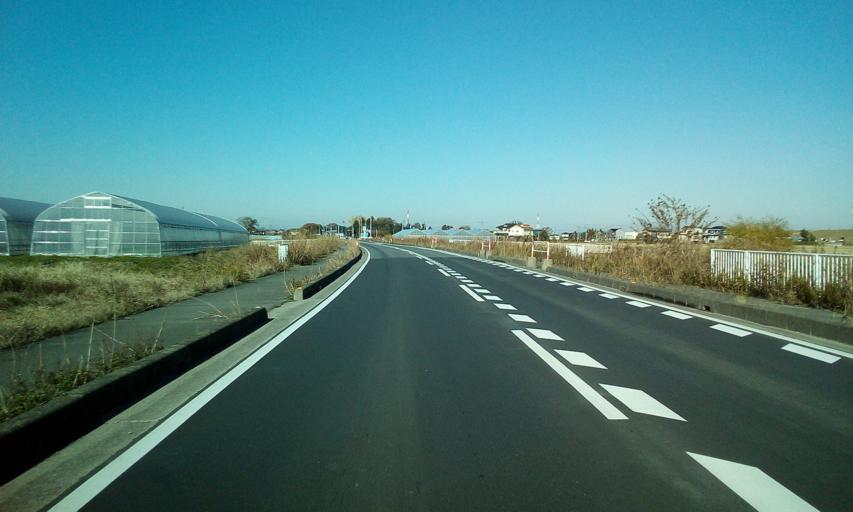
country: JP
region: Chiba
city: Nagareyama
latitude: 35.8842
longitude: 139.8865
